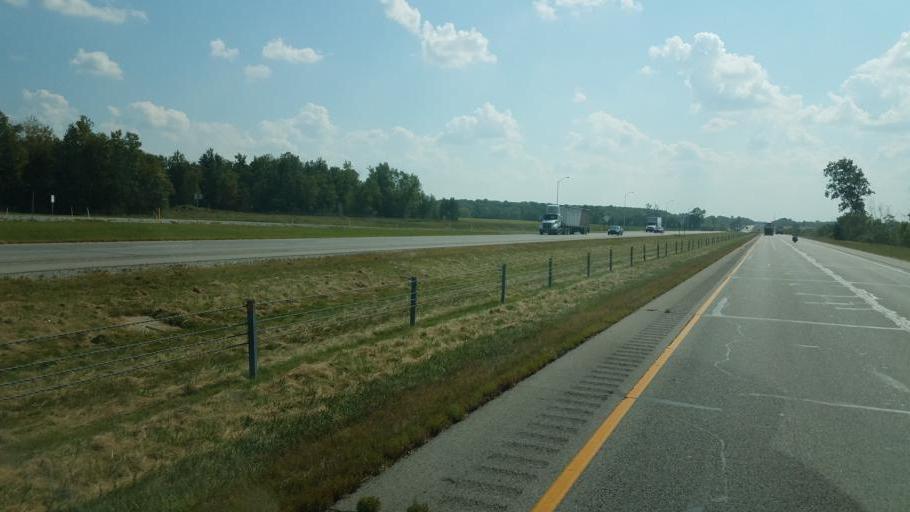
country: US
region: Indiana
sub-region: DeKalb County
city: Garrett
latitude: 41.2953
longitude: -85.0875
